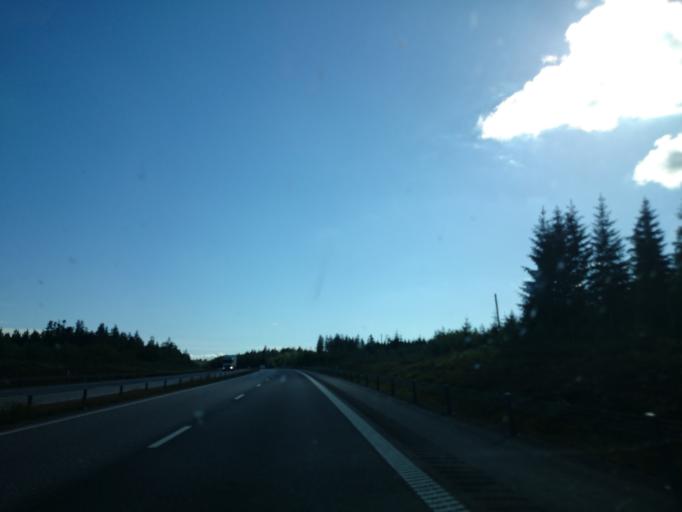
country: SE
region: Kronoberg
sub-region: Markaryds Kommun
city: Stromsnasbruk
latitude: 56.5161
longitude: 13.6659
